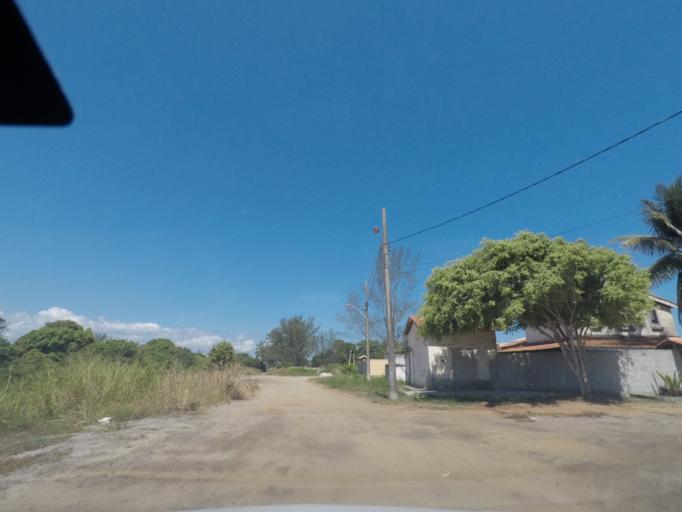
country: BR
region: Rio de Janeiro
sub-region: Marica
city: Marica
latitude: -22.9726
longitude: -42.9200
